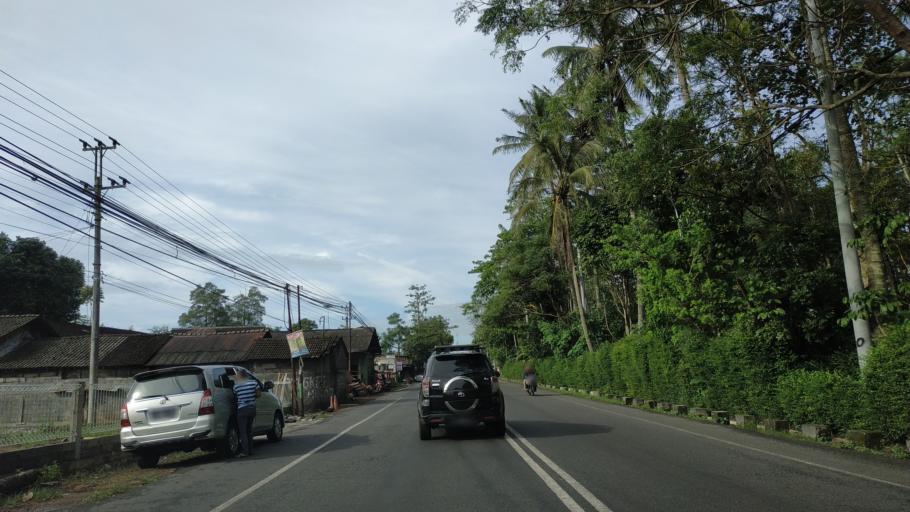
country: ID
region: Central Java
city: Salatiga
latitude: -7.3805
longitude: 110.5150
